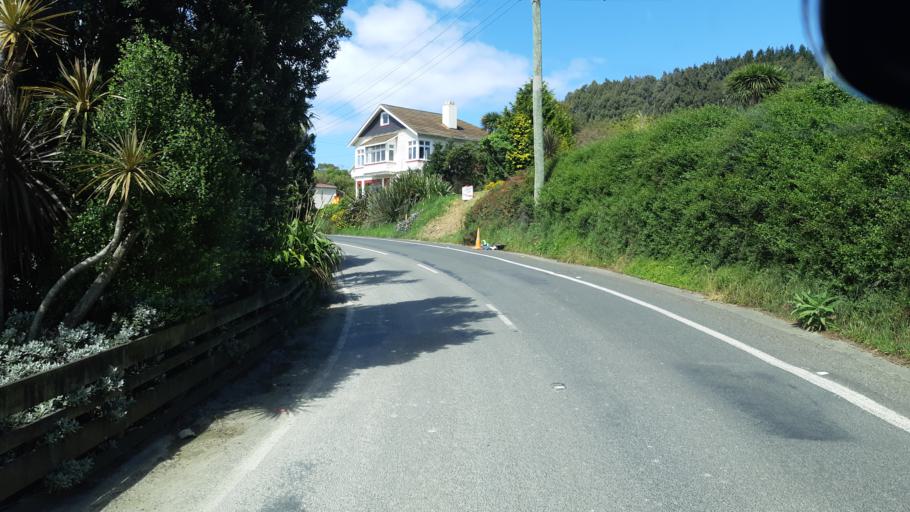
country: NZ
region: Otago
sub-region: Dunedin City
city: Portobello
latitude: -45.8484
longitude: 170.6207
